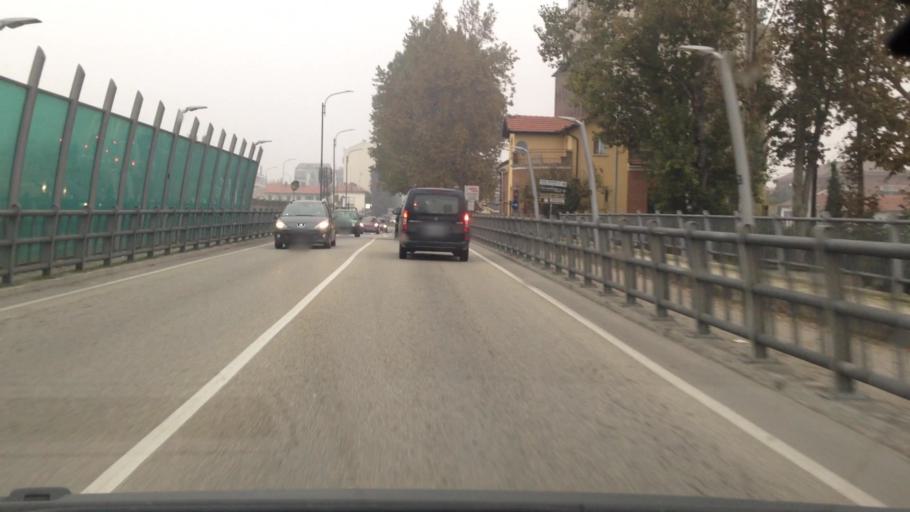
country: IT
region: Piedmont
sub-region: Provincia di Asti
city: Asti
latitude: 44.8853
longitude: 8.2122
